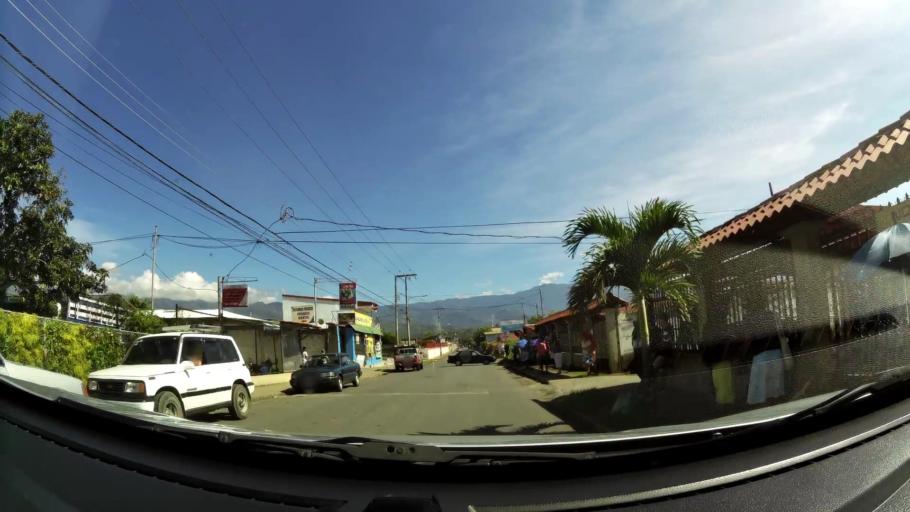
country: CR
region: San Jose
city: San Isidro
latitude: 9.3735
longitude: -83.7094
